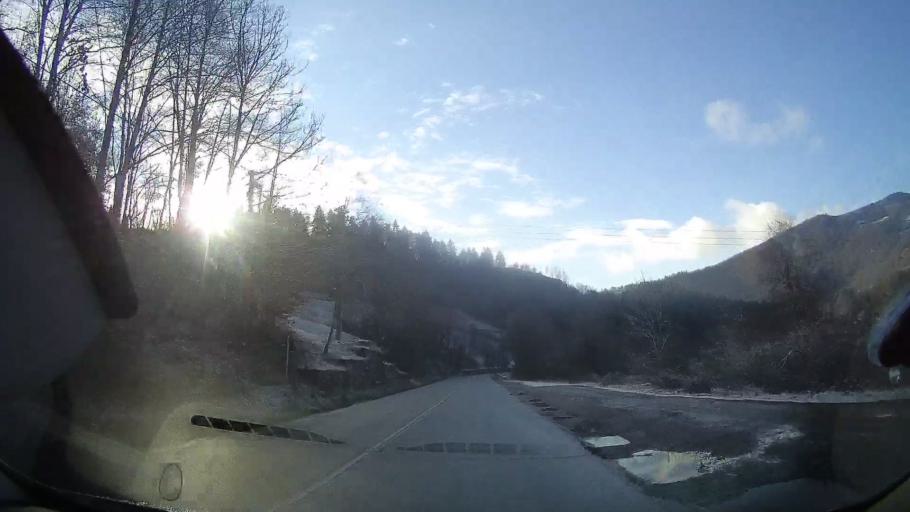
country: RO
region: Alba
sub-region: Comuna Sohodol
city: Sohodol
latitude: 46.3660
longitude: 23.0293
